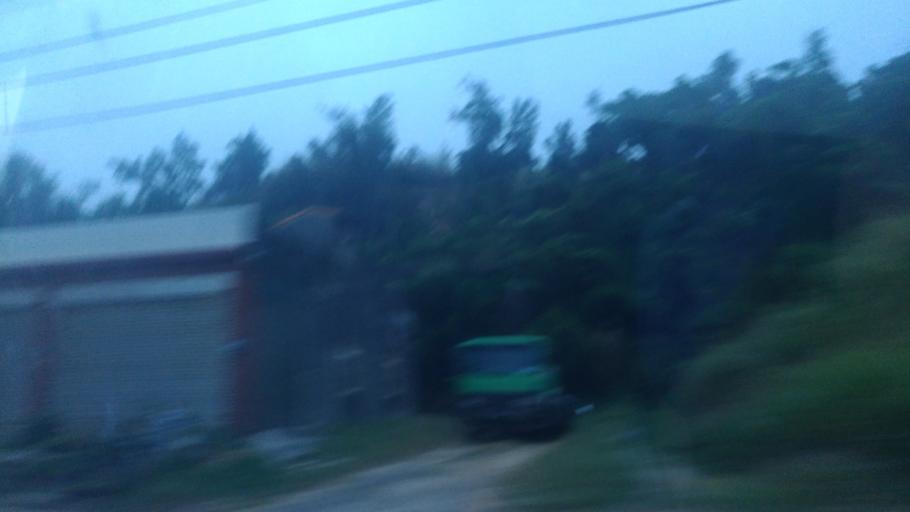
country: TW
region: Taiwan
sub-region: Miaoli
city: Miaoli
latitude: 24.5680
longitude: 120.7117
